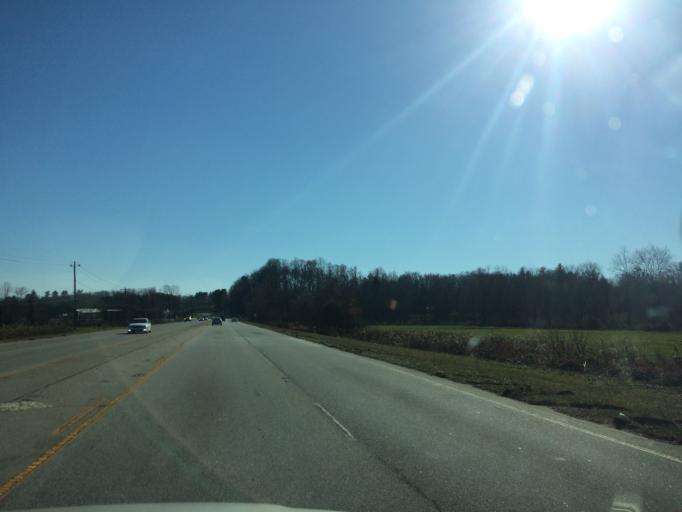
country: US
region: North Carolina
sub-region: Henderson County
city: Mills River
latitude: 35.3947
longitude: -82.5690
